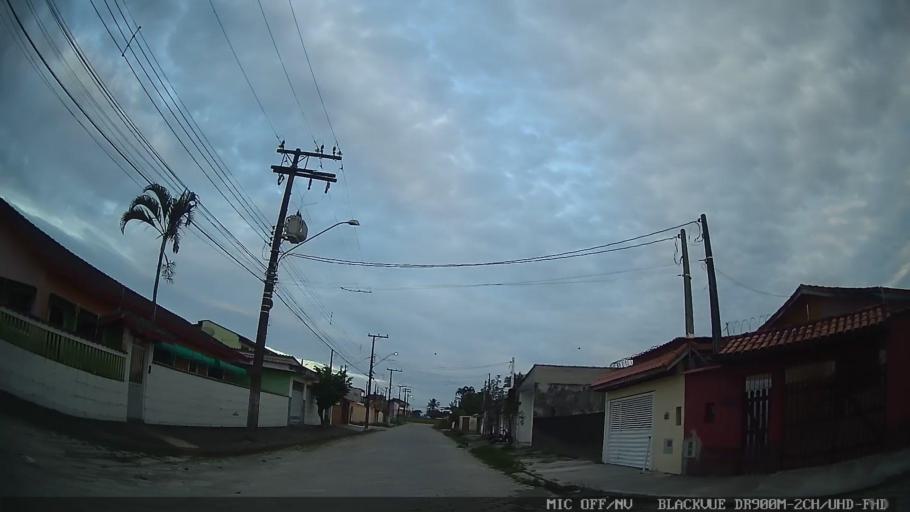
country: BR
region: Sao Paulo
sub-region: Itanhaem
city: Itanhaem
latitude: -24.1721
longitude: -46.7783
